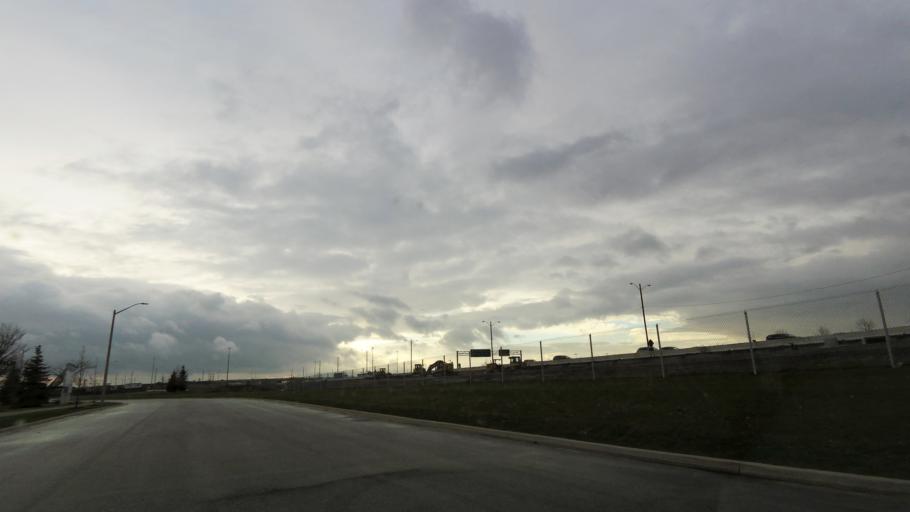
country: CA
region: Ontario
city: Mississauga
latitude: 43.6224
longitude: -79.7012
